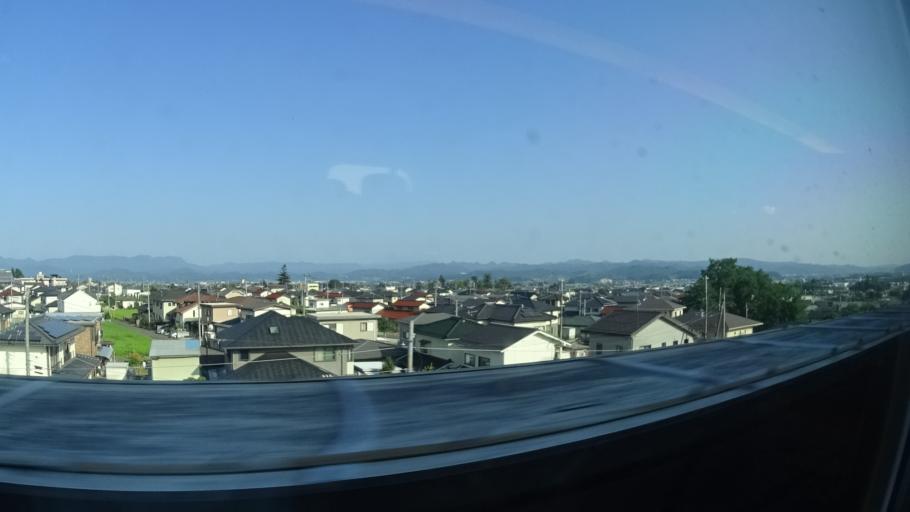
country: JP
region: Fukushima
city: Hobaramachi
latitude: 37.8493
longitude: 140.5126
